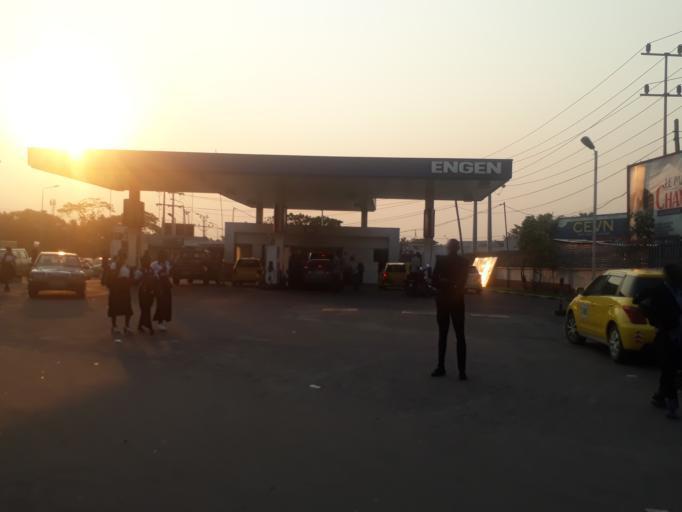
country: CD
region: Kinshasa
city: Kinshasa
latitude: -4.3378
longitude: 15.3050
